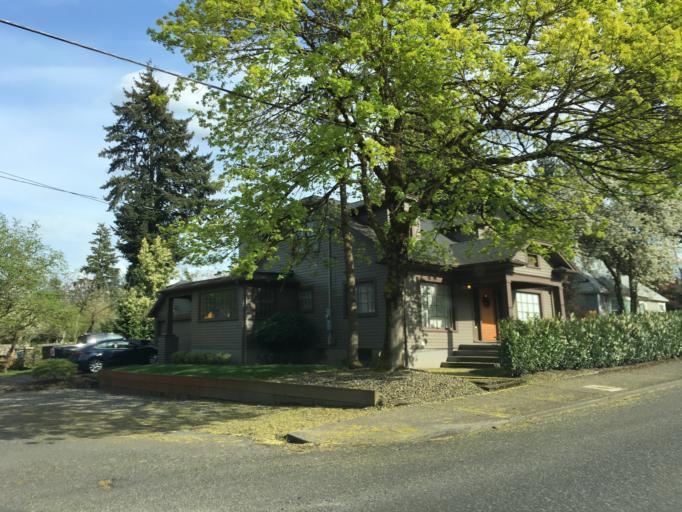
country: US
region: Oregon
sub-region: Multnomah County
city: Lents
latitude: 45.5498
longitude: -122.5578
